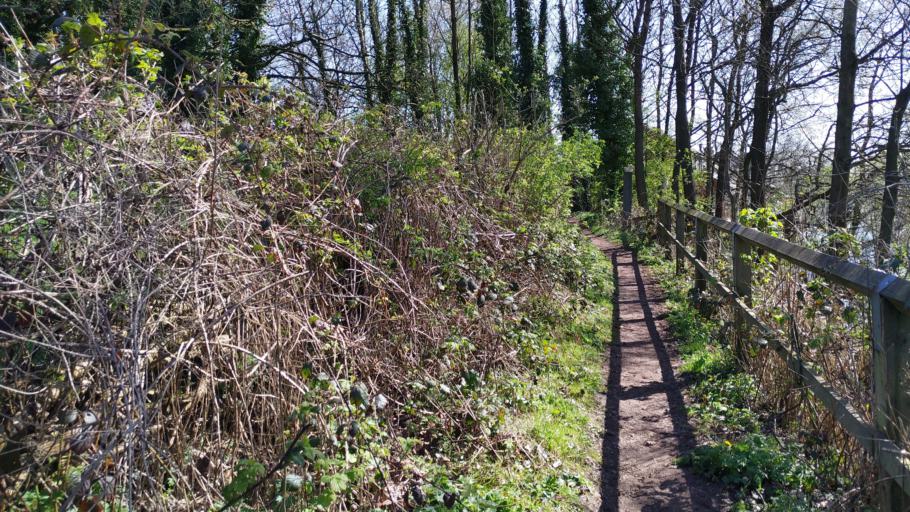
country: GB
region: England
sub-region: Lancashire
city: Chorley
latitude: 53.6809
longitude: -2.6199
